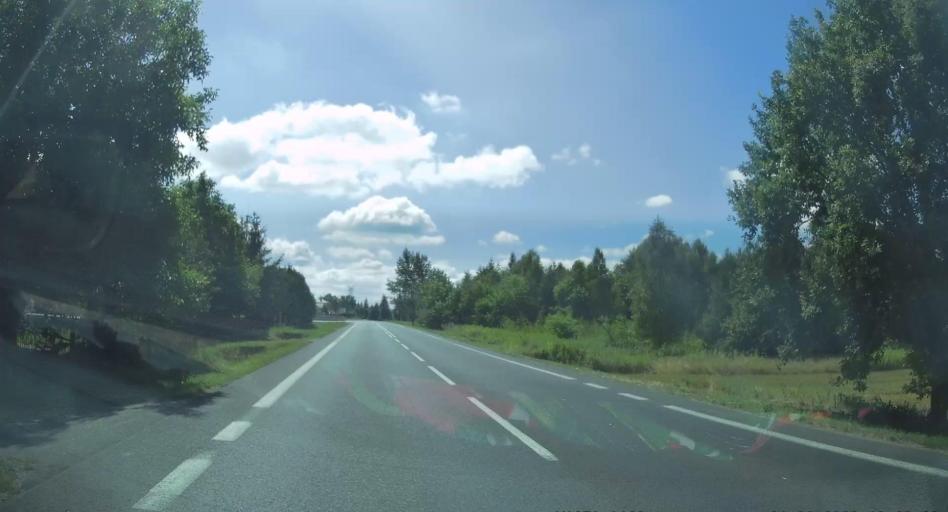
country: PL
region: Subcarpathian Voivodeship
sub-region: Powiat debicki
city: Brzeznica
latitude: 50.1342
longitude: 21.4853
